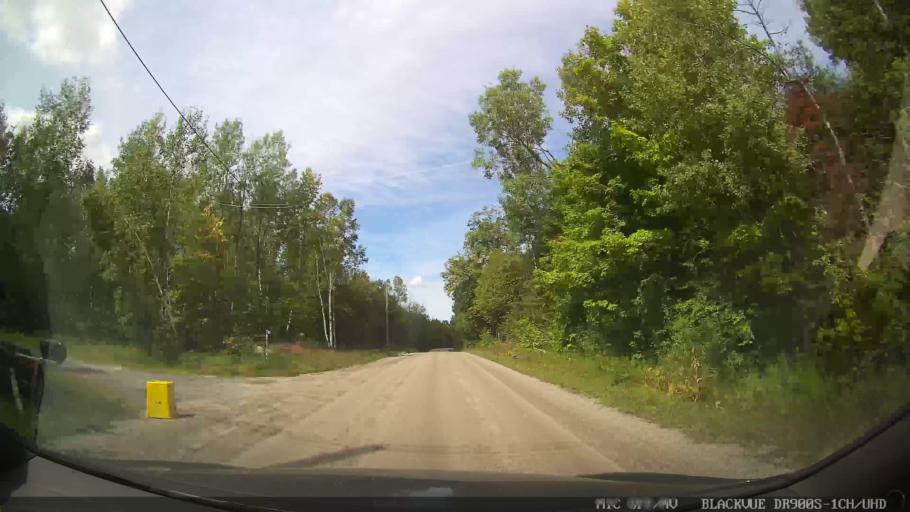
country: CA
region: Ontario
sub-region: Lanark County
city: Smiths Falls
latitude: 44.9550
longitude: -75.8850
